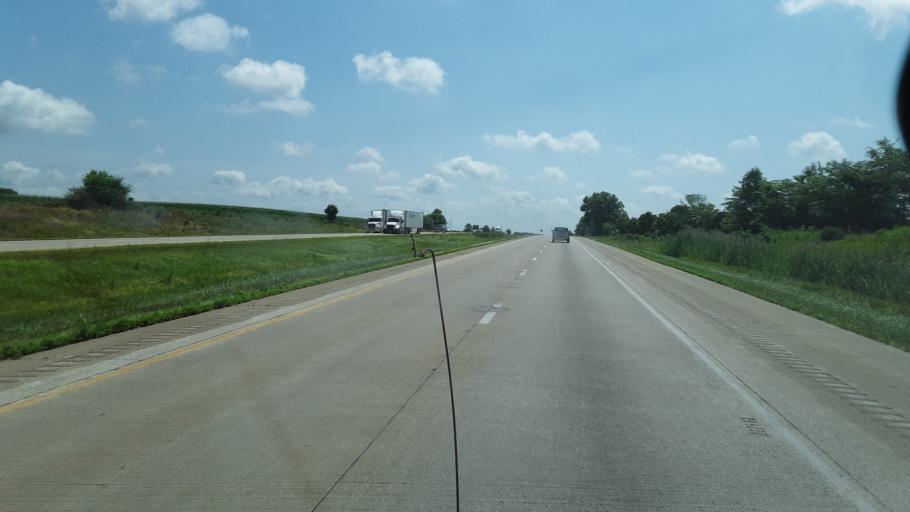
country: US
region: Illinois
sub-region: Clark County
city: Marshall
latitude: 39.4216
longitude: -87.6421
